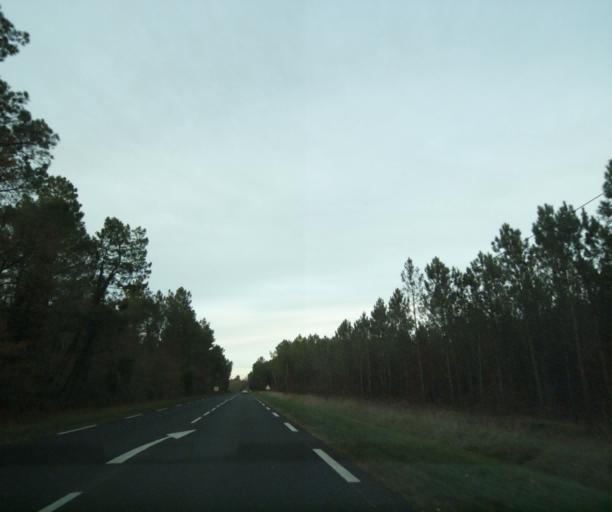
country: FR
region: Aquitaine
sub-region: Departement de la Gironde
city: Bazas
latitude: 44.3541
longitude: -0.2371
